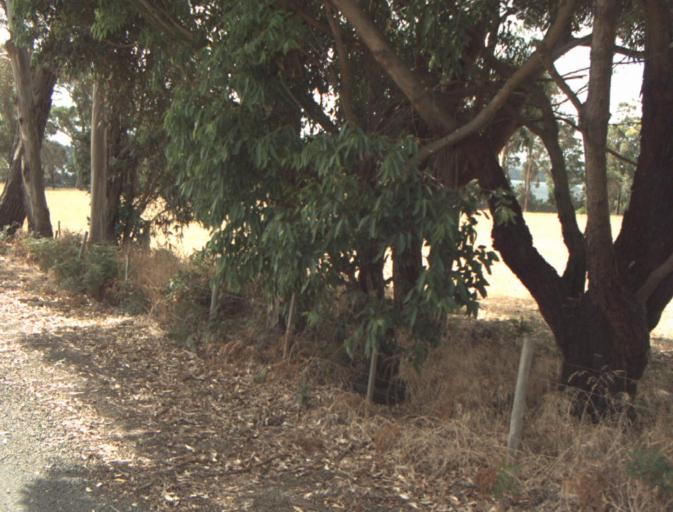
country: AU
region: Tasmania
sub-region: Launceston
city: Mayfield
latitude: -41.2990
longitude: 146.9902
